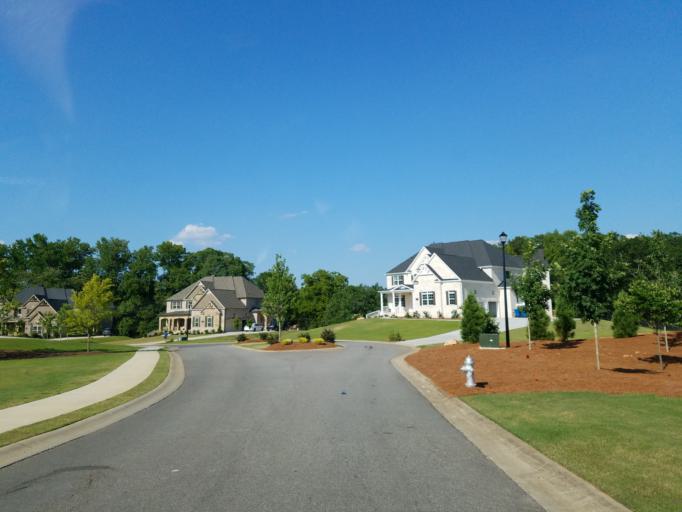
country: US
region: Georgia
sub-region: Fulton County
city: Milton
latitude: 34.1808
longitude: -84.3254
